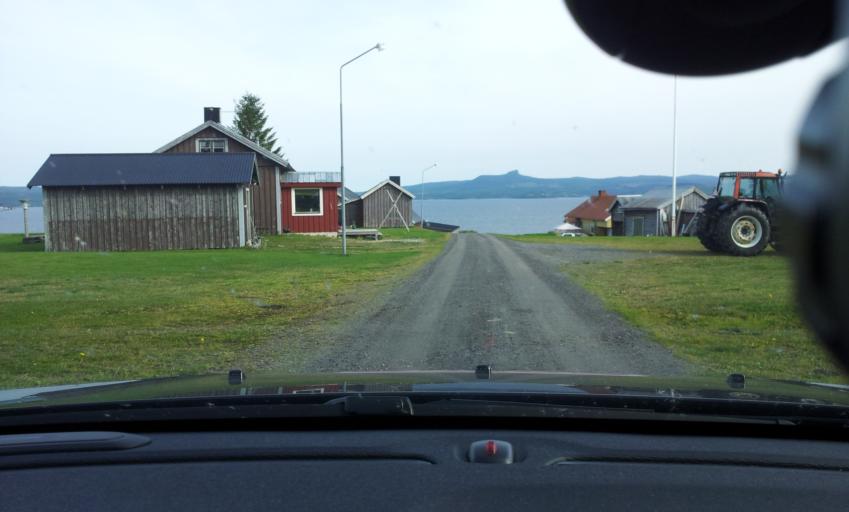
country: SE
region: Jaemtland
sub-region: Are Kommun
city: Are
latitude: 63.6223
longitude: 12.9171
